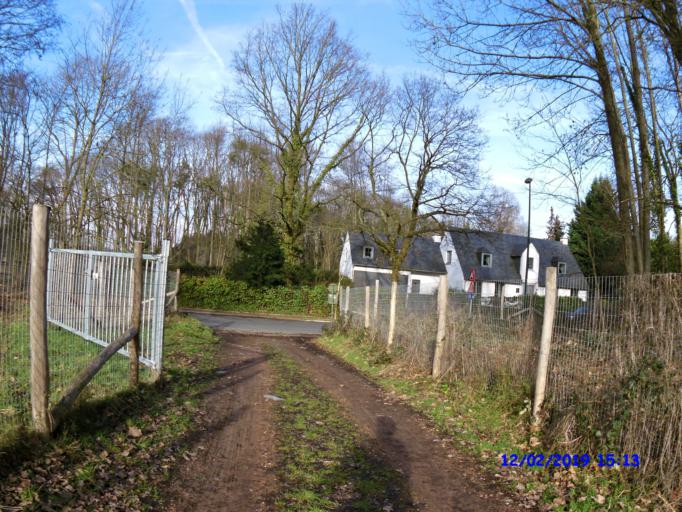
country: BE
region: Flanders
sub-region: Provincie Vlaams-Brabant
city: Sint-Genesius-Rode
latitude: 50.7612
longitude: 4.3654
